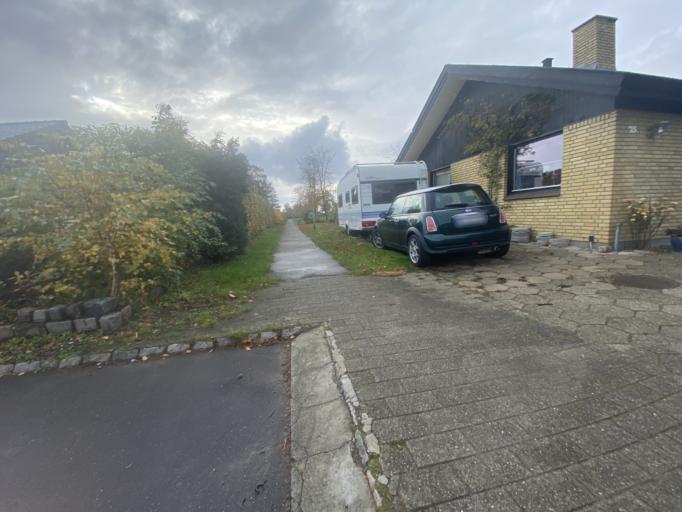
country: DK
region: Capital Region
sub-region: Dragor Kommune
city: Dragor
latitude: 55.5919
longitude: 12.6497
